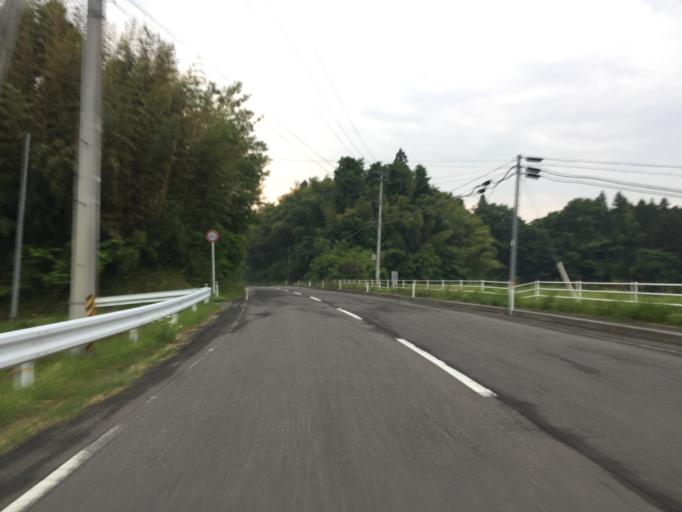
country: JP
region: Fukushima
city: Ishikawa
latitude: 37.2102
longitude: 140.4461
